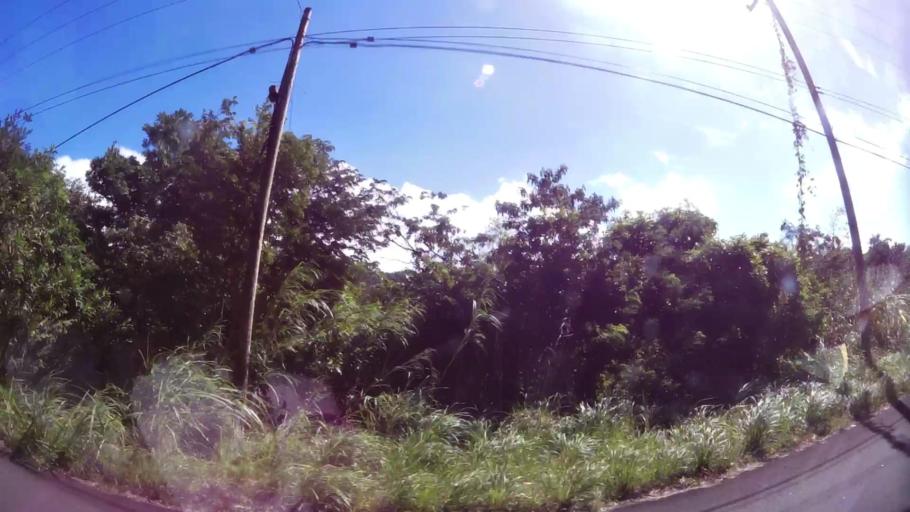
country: DM
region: Saint Paul
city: Pont Casse
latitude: 15.3476
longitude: -61.3627
